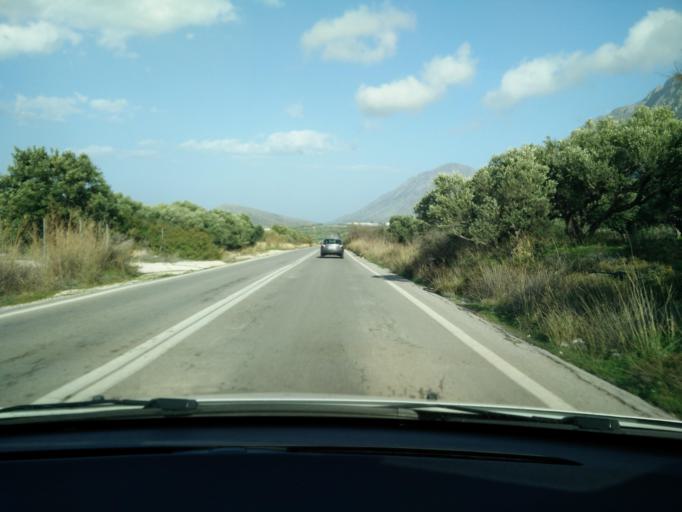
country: GR
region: Crete
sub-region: Nomos Lasithiou
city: Kato Chorio
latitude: 35.0757
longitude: 25.8087
